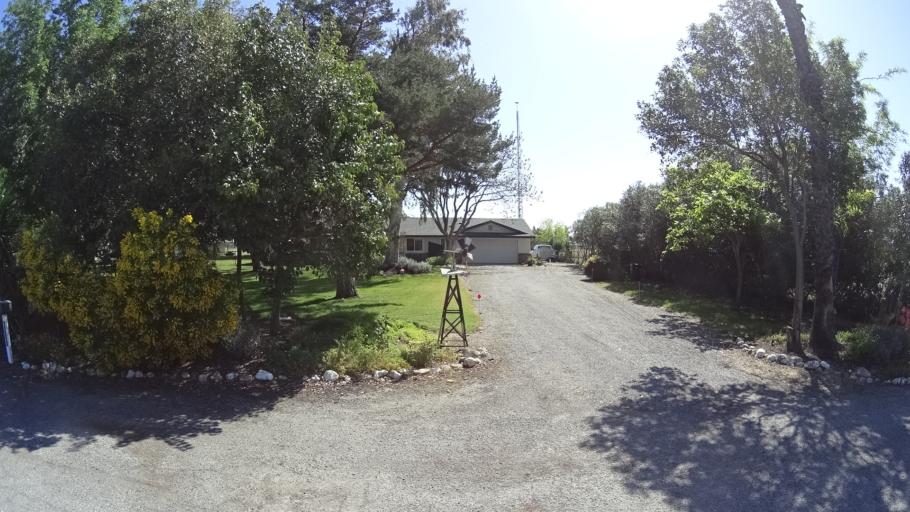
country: US
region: California
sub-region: Glenn County
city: Orland
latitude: 39.7294
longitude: -122.1909
